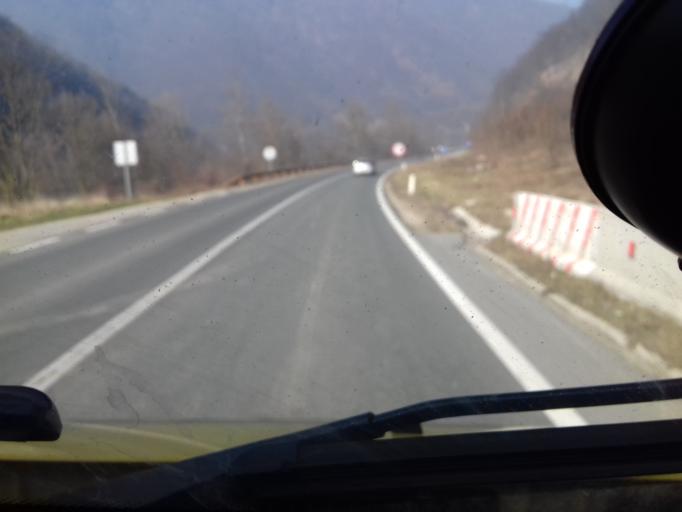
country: BA
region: Federation of Bosnia and Herzegovina
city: Busovaca
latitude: 44.1342
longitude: 17.9361
